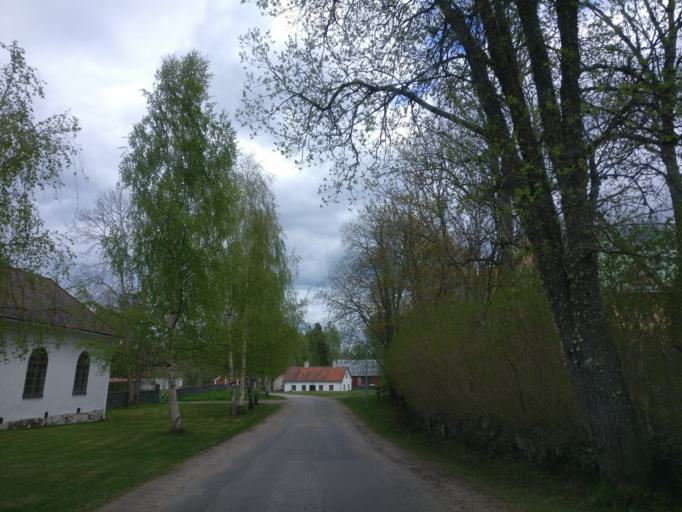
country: SE
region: Gaevleborg
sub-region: Soderhamns Kommun
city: Marielund
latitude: 61.4595
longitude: 17.1225
